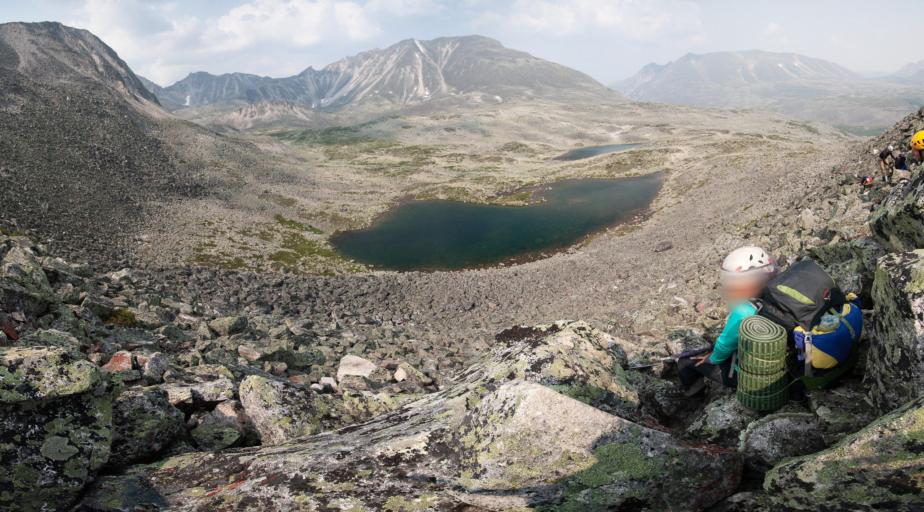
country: RU
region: Respublika Buryatiya
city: Novyy Uoyan
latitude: 56.2145
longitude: 111.0268
